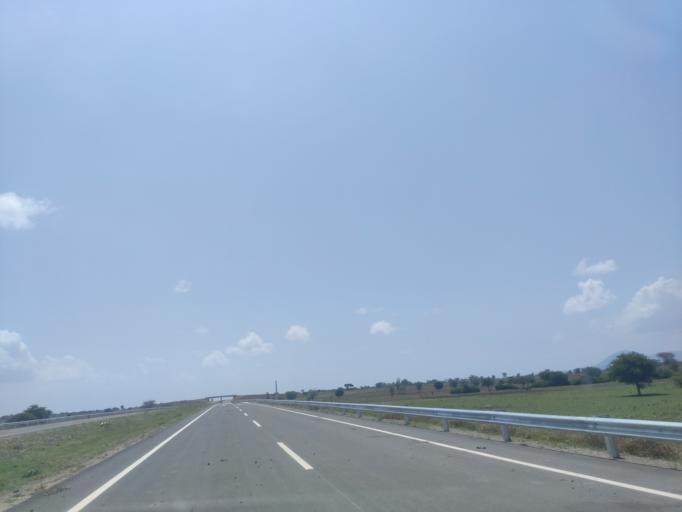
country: ET
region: Oromiya
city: Ziway
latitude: 8.2376
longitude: 38.8786
